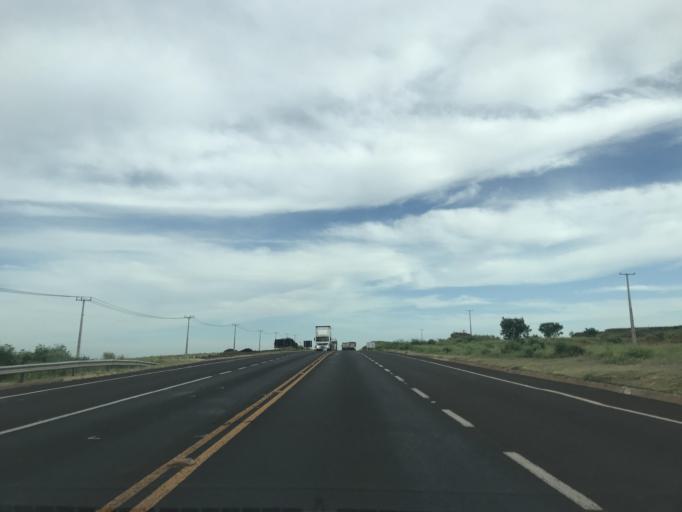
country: BR
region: Parana
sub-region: Paranavai
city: Paranavai
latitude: -23.0363
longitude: -52.4778
